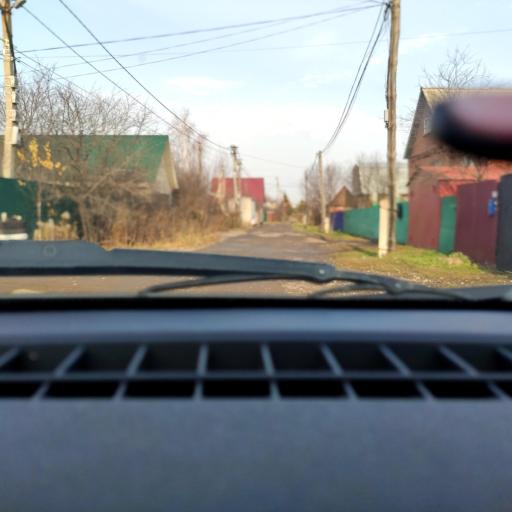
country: RU
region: Bashkortostan
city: Iglino
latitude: 54.8207
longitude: 56.1844
